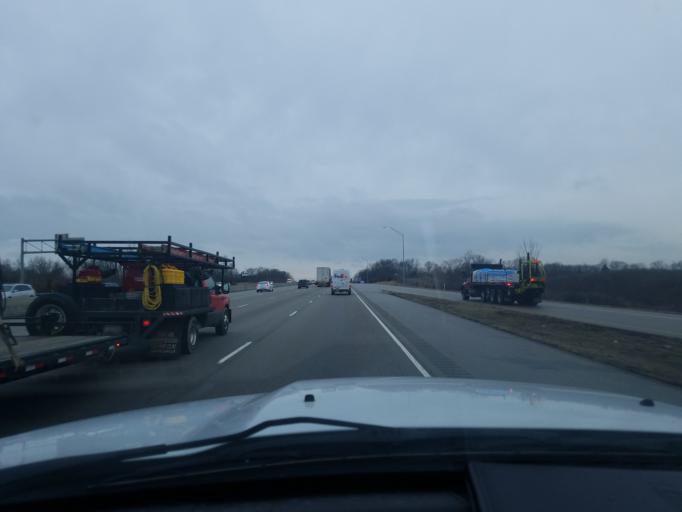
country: US
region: Ohio
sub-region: Warren County
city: Franklin
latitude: 39.5402
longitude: -84.2976
